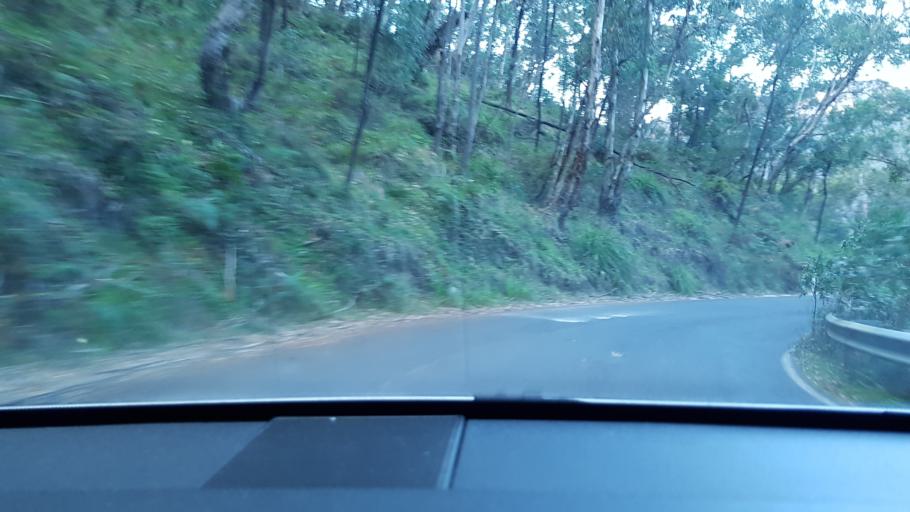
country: AU
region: New South Wales
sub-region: Lithgow
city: Portland
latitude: -33.3096
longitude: 150.1121
